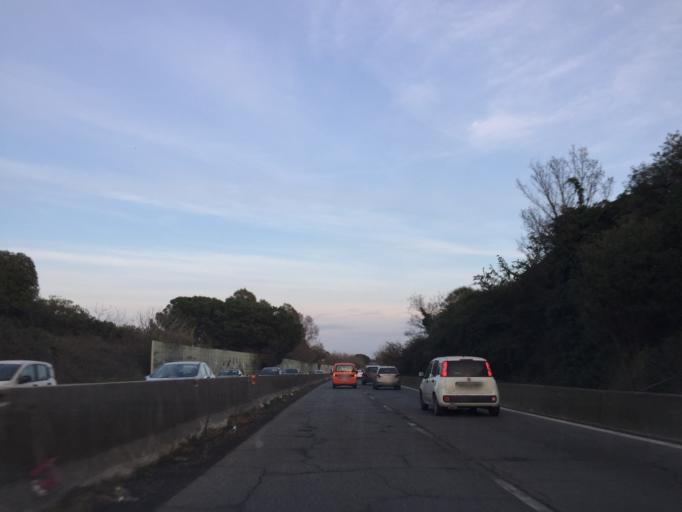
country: IT
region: Latium
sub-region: Citta metropolitana di Roma Capitale
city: Formello
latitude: 42.0447
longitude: 12.4038
